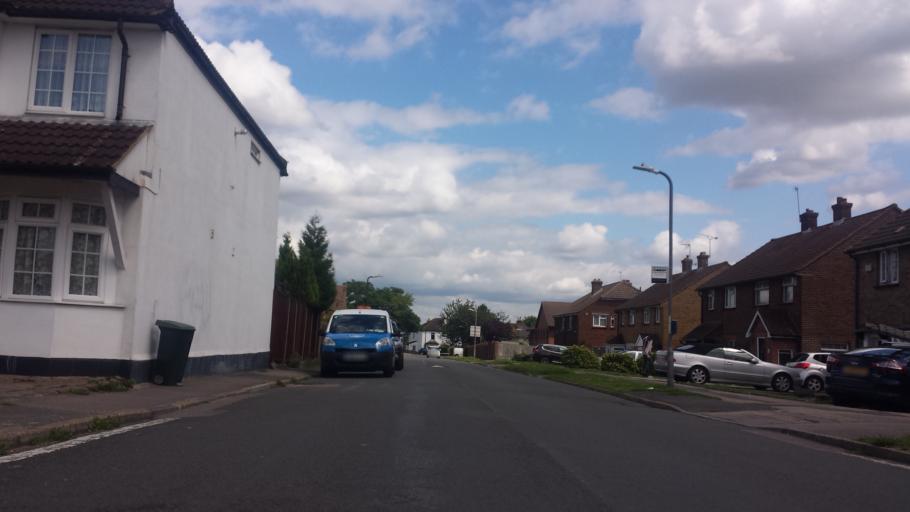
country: GB
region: England
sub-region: Kent
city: Swanley
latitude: 51.4006
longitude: 0.1637
